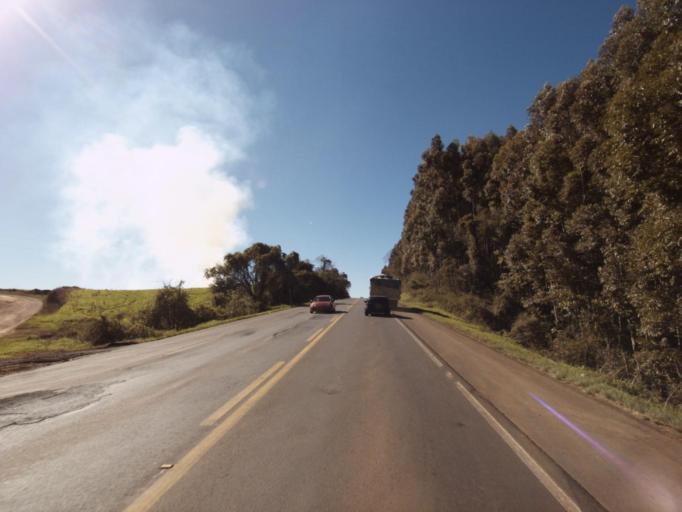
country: BR
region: Santa Catarina
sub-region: Xanxere
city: Xanxere
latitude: -26.9226
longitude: -52.4961
